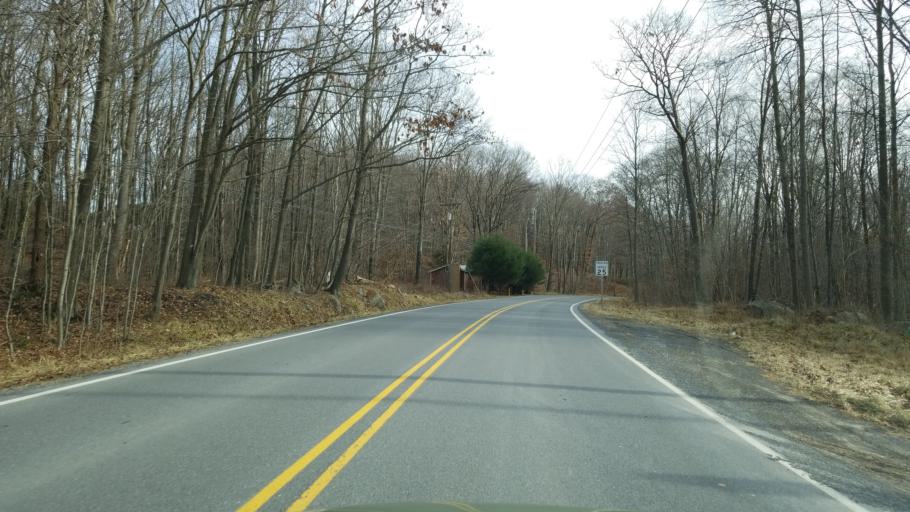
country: US
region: Pennsylvania
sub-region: Indiana County
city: Johnsonburg
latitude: 40.8904
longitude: -78.7822
